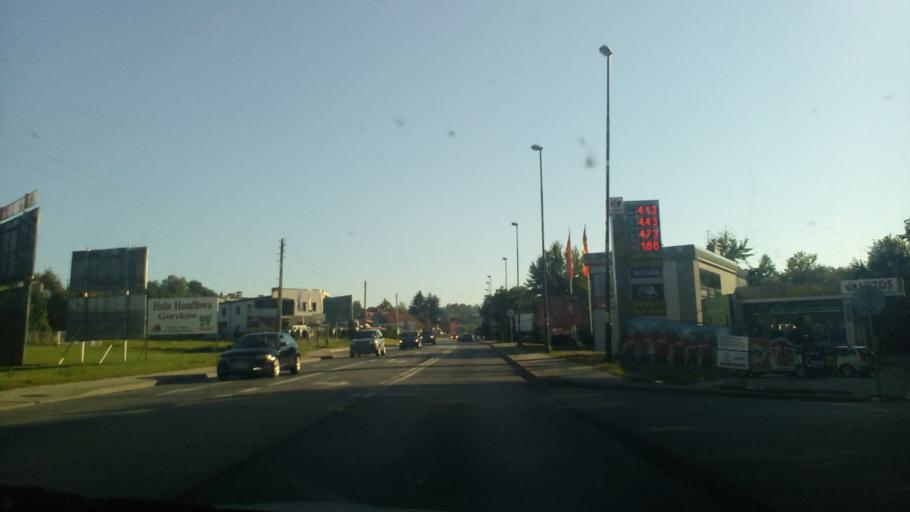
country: PL
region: Lesser Poland Voivodeship
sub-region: Powiat nowosadecki
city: Stary Sacz
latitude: 49.5853
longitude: 20.6729
